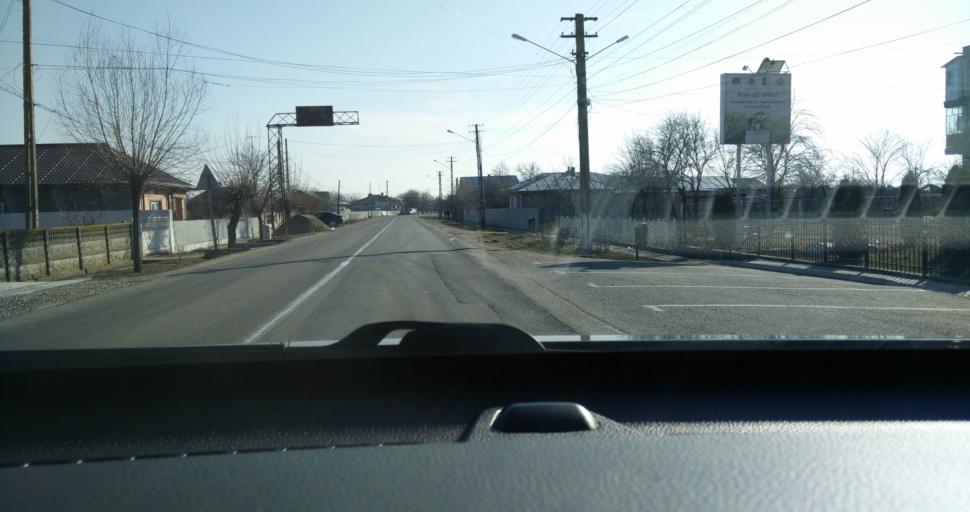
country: RO
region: Vrancea
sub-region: Comuna Nanesti
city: Nanesti
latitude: 45.5500
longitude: 27.5006
